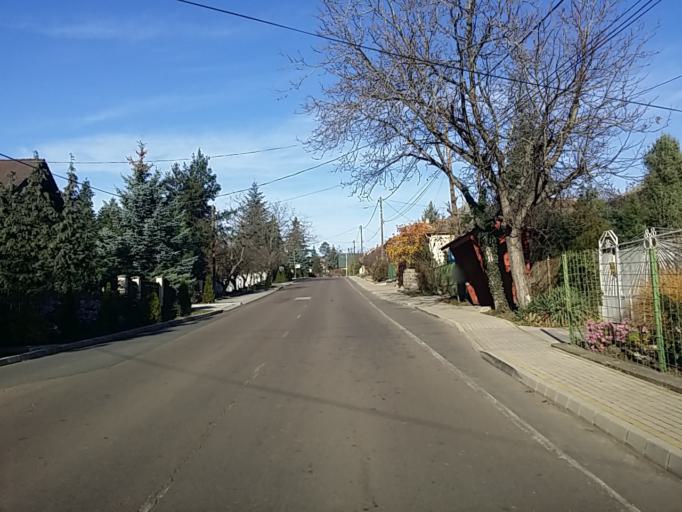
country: HU
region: Heves
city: Abasar
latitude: 47.8121
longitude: 20.0027
